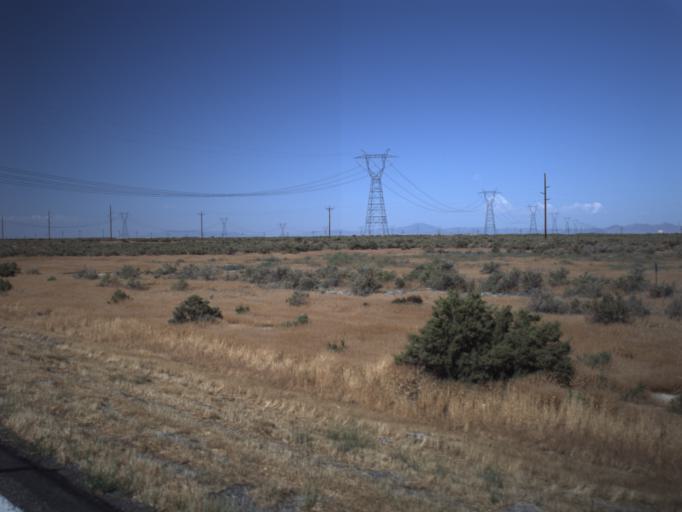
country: US
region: Utah
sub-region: Millard County
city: Delta
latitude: 39.4931
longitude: -112.3999
